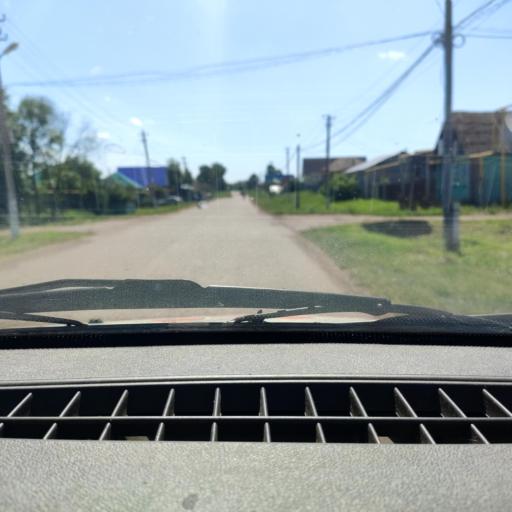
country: RU
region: Bashkortostan
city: Blagoveshchensk
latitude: 55.1003
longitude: 55.8531
